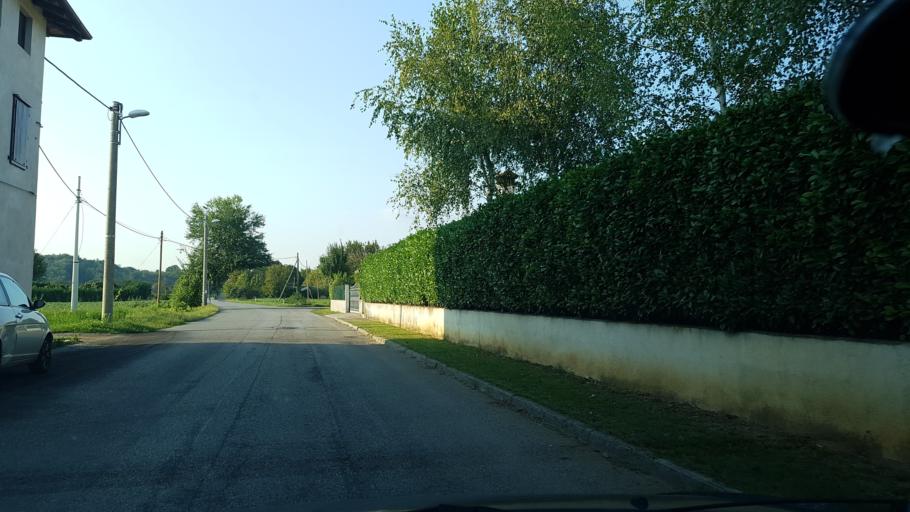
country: IT
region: Friuli Venezia Giulia
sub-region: Provincia di Gorizia
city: Mossa
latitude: 45.9411
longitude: 13.5750
